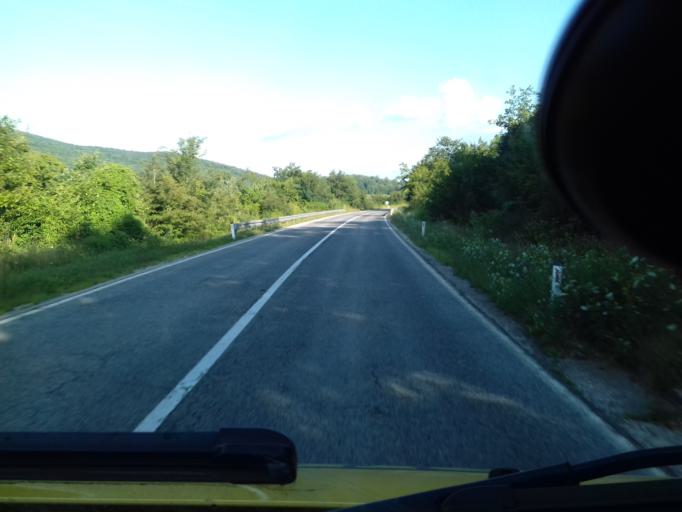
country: BA
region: Federation of Bosnia and Herzegovina
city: Orasac
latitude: 44.6604
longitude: 16.1508
